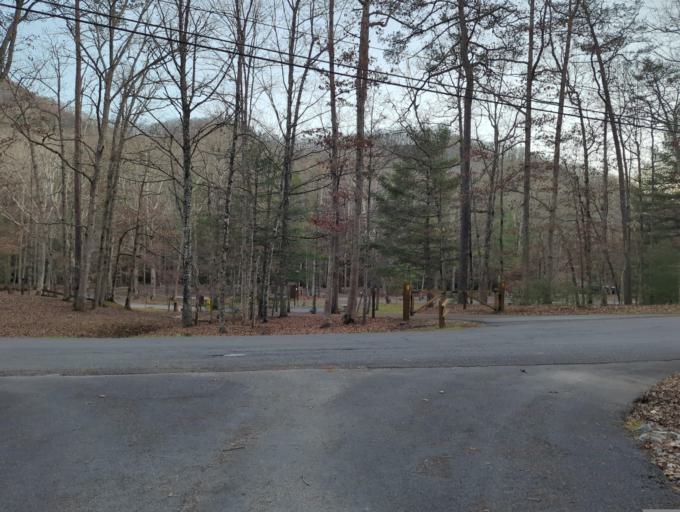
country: US
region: Virginia
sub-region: Smyth County
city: Marion
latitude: 36.8907
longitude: -81.5201
